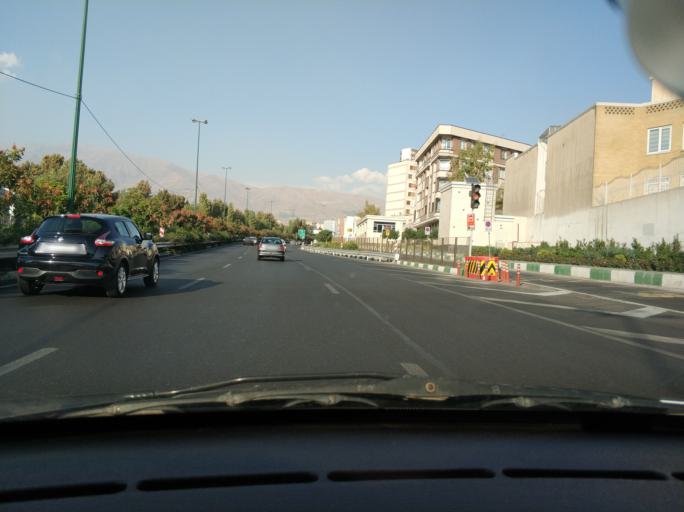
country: IR
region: Tehran
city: Tajrish
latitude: 35.7710
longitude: 51.4725
